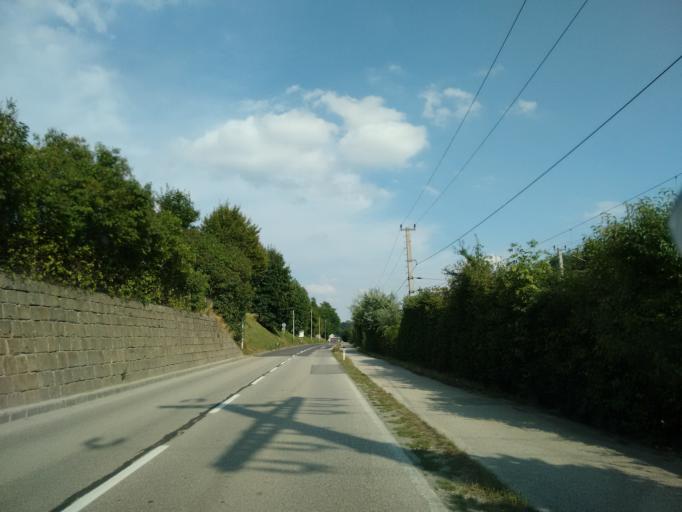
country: AT
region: Upper Austria
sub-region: Politischer Bezirk Grieskirchen
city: Bad Schallerbach
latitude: 48.2282
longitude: 13.9269
